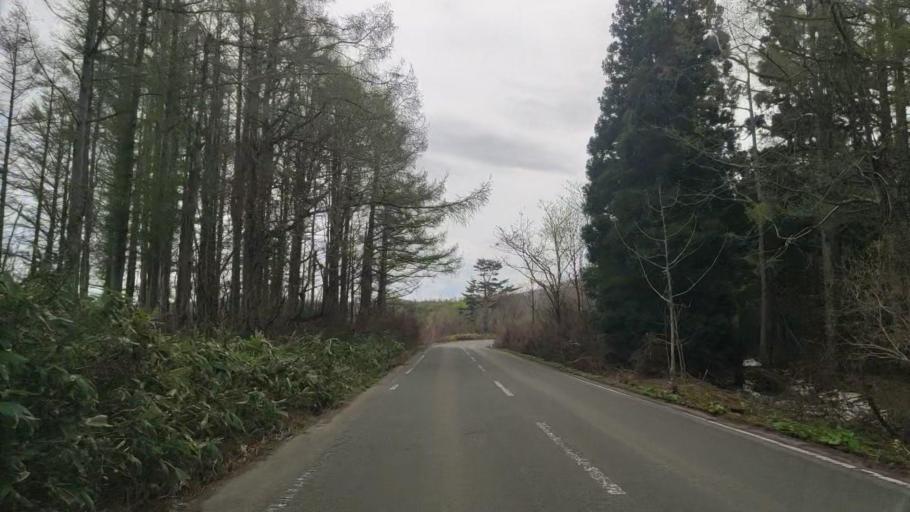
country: JP
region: Aomori
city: Aomori Shi
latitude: 40.7278
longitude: 140.8478
